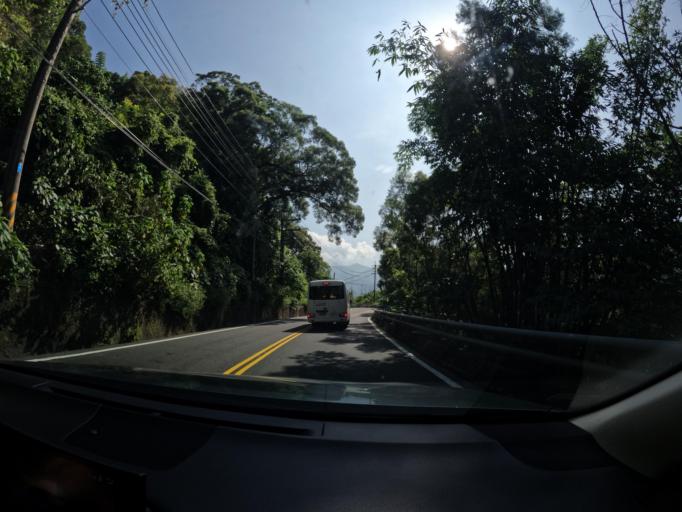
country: TW
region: Taiwan
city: Yujing
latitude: 23.0699
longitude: 120.6368
